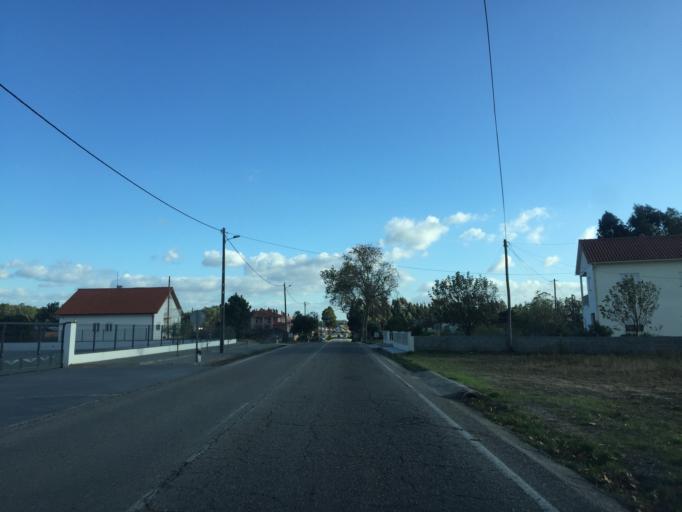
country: PT
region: Leiria
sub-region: Pombal
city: Lourical
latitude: 39.9630
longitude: -8.7898
